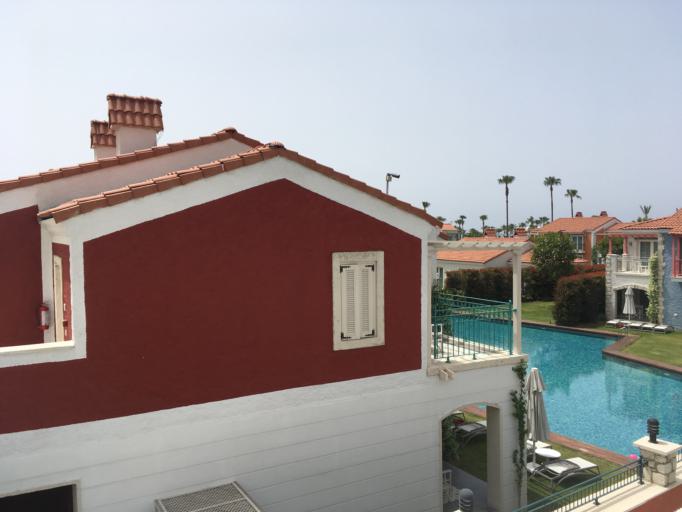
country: TR
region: Antalya
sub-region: Serik
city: Kumkoey
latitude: 36.8605
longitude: 30.9896
